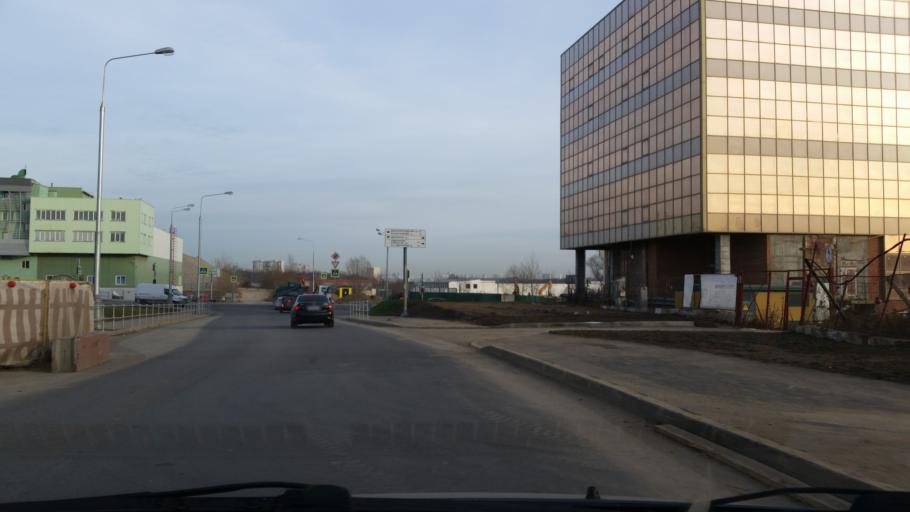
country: RU
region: Moscow
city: Tsaritsyno
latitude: 55.6136
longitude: 37.6263
